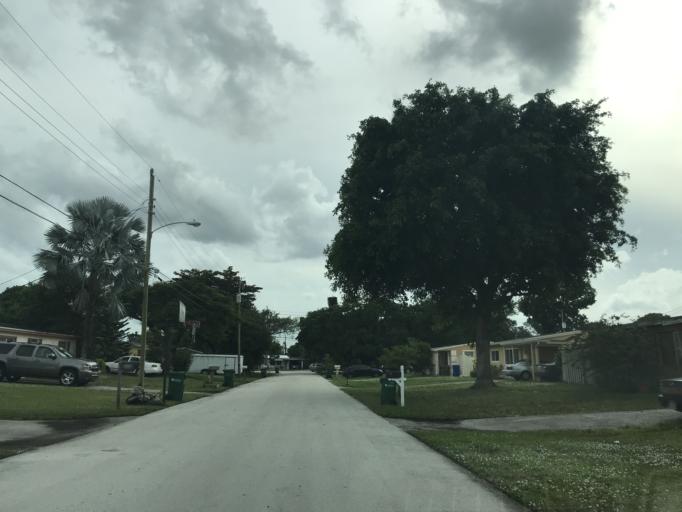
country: US
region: Florida
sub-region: Broward County
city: Margate
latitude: 26.2596
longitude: -80.2048
